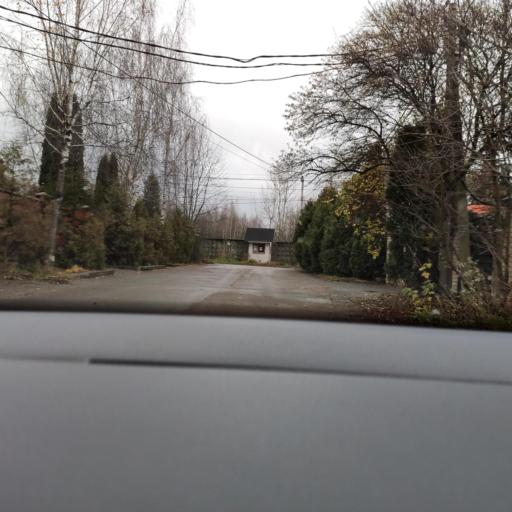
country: RU
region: Moscow
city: Gol'yanovo
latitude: 55.8341
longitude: 37.8331
